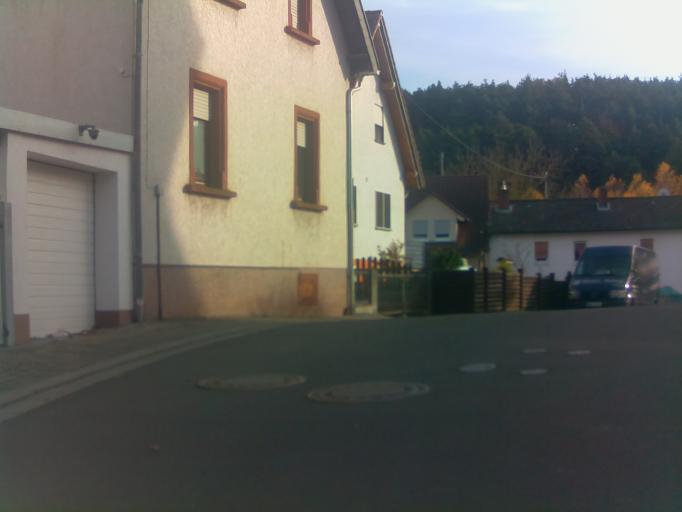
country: DE
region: Rheinland-Pfalz
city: Carlsberg
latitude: 49.4917
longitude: 8.0306
